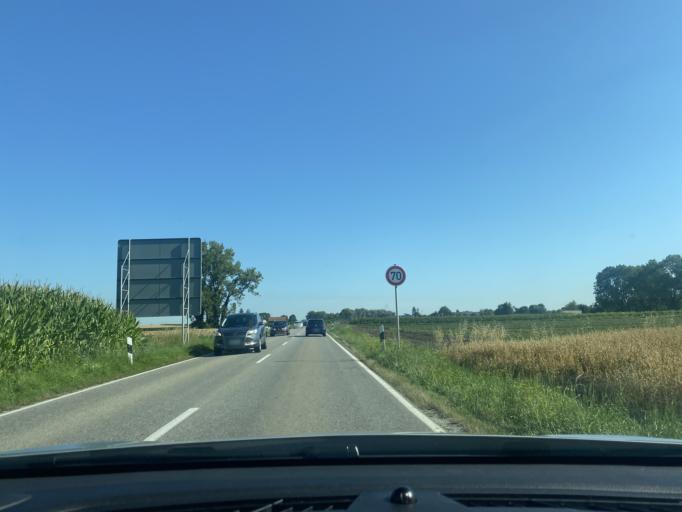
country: DE
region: Bavaria
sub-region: Upper Bavaria
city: Erding
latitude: 48.3176
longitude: 11.8934
